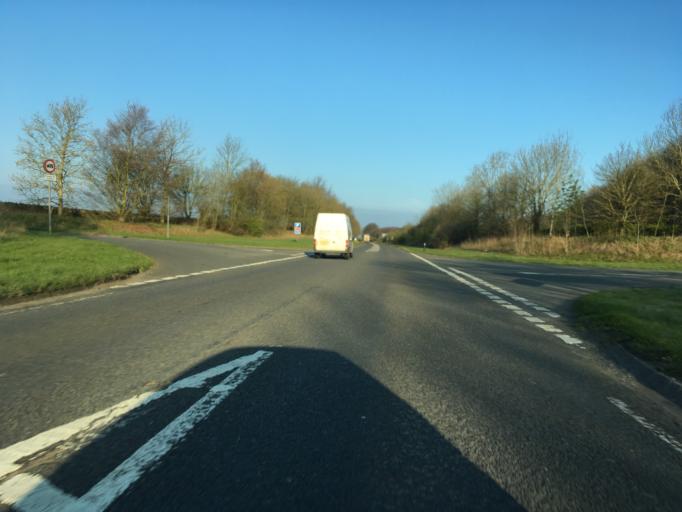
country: GB
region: England
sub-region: Gloucestershire
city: Northleach
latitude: 51.8446
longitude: -1.8598
